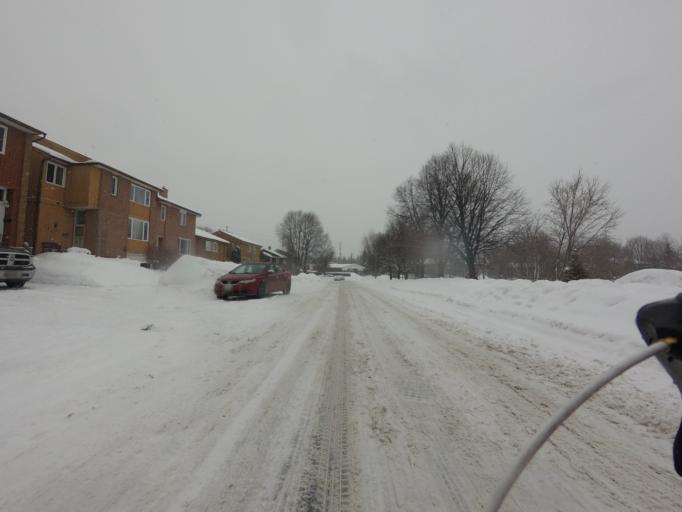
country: CA
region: Ontario
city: Ottawa
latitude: 45.3645
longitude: -75.6818
